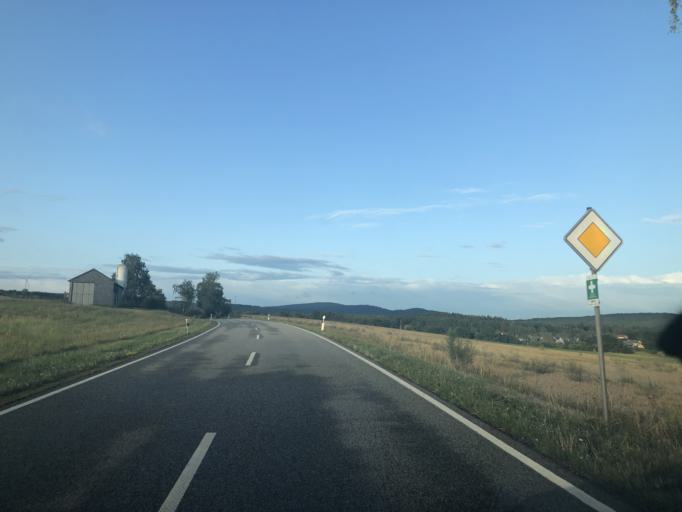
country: DE
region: Rheinland-Pfalz
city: Grimburg
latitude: 49.5992
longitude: 6.9124
